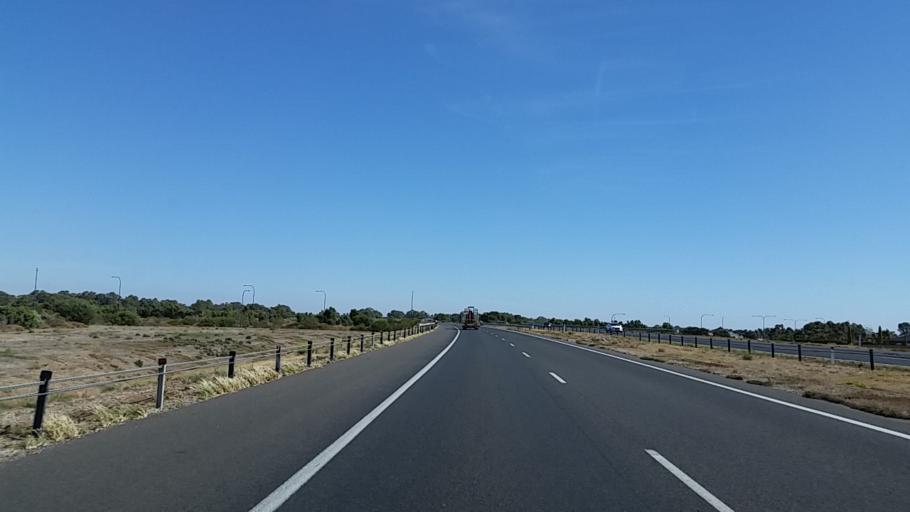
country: AU
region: South Australia
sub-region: Playford
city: Angle Vale
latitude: -34.6087
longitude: 138.6889
